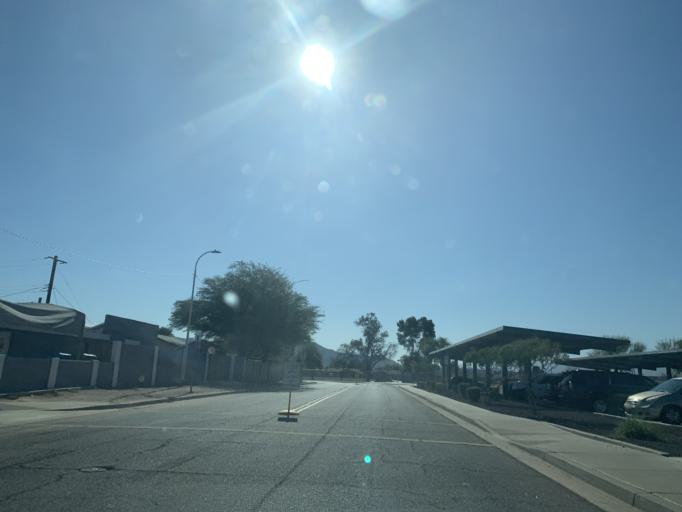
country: US
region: Arizona
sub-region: Maricopa County
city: Laveen
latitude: 33.4002
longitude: -112.1402
